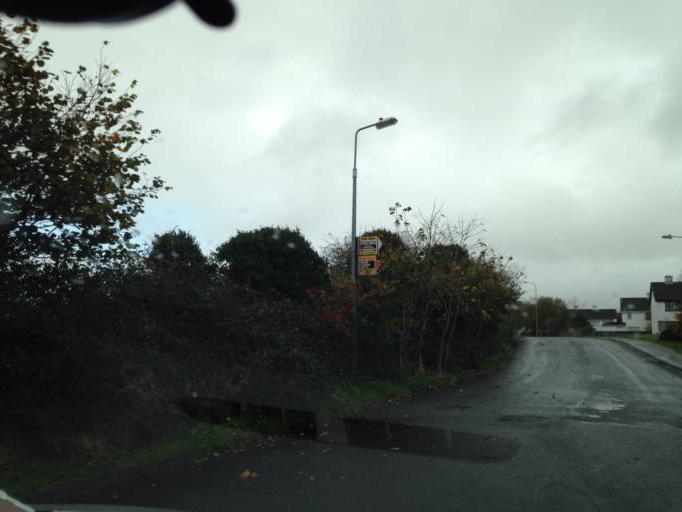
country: IE
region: Connaught
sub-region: County Galway
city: Gaillimh
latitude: 53.2731
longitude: -9.0092
